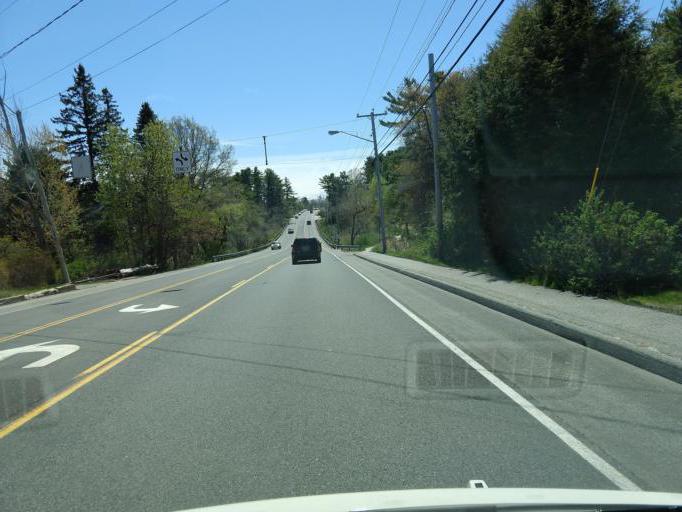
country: US
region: Maine
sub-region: York County
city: Wells Beach Station
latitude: 43.2994
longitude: -70.5870
